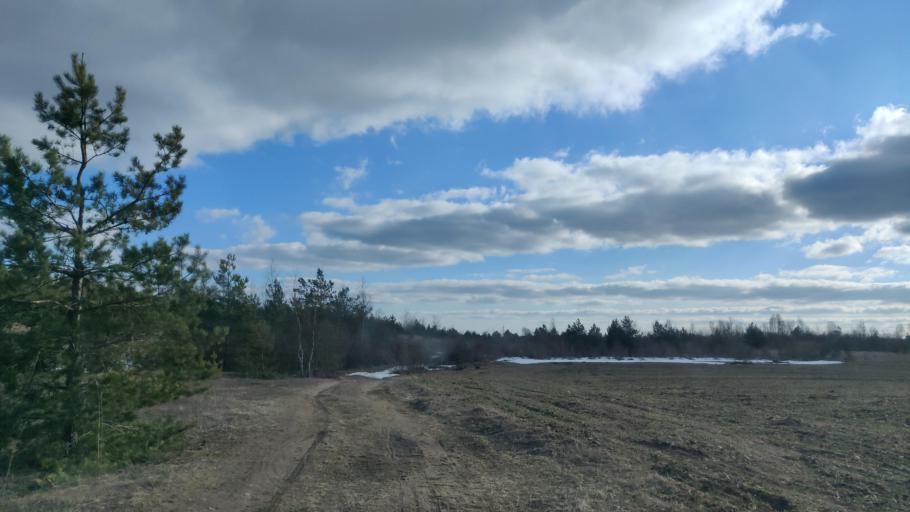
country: LT
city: Lentvaris
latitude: 54.6147
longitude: 24.9989
